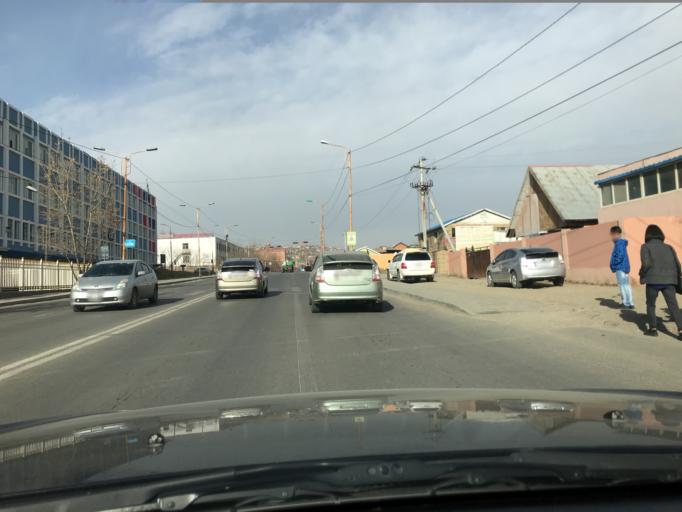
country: MN
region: Ulaanbaatar
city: Ulaanbaatar
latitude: 47.9293
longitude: 106.8902
